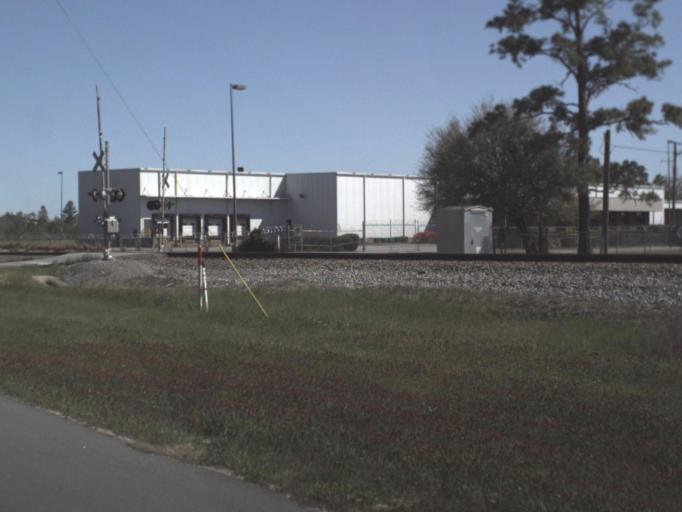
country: US
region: Florida
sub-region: Walton County
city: DeFuniak Springs
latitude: 30.7375
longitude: -86.1680
